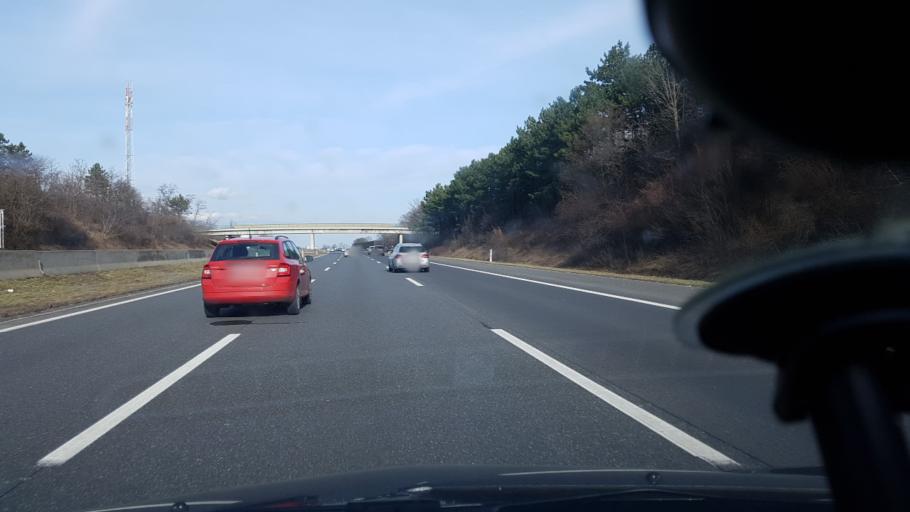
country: AT
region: Lower Austria
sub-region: Politischer Bezirk Wiener Neustadt
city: Theresienfeld
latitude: 47.8737
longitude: 16.1985
